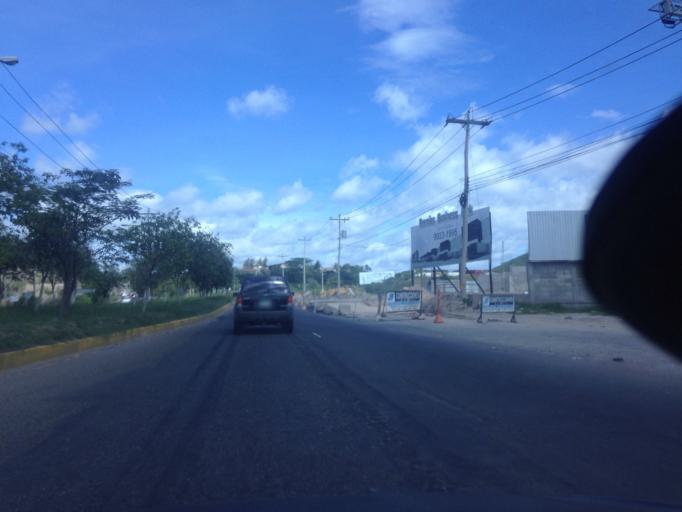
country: HN
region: Francisco Morazan
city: El Tablon
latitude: 14.0469
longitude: -87.1909
